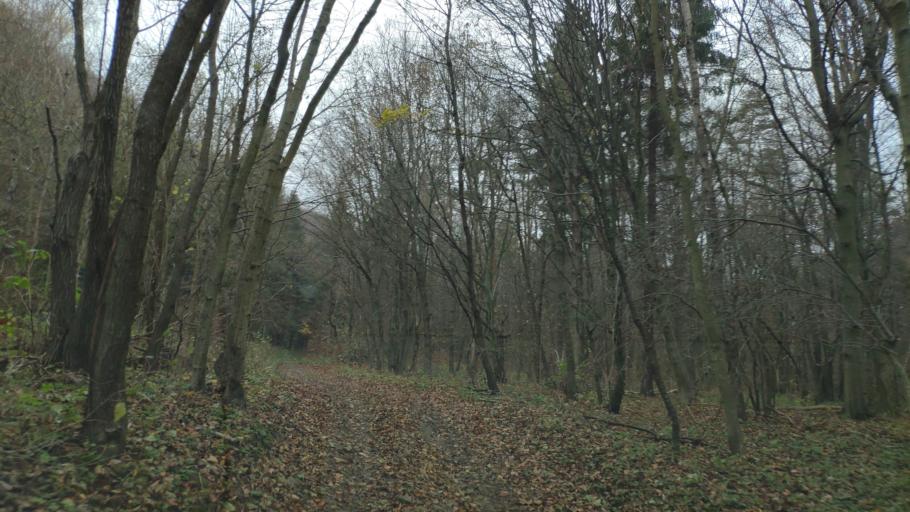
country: SK
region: Presovsky
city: Sabinov
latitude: 49.1433
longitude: 21.2143
